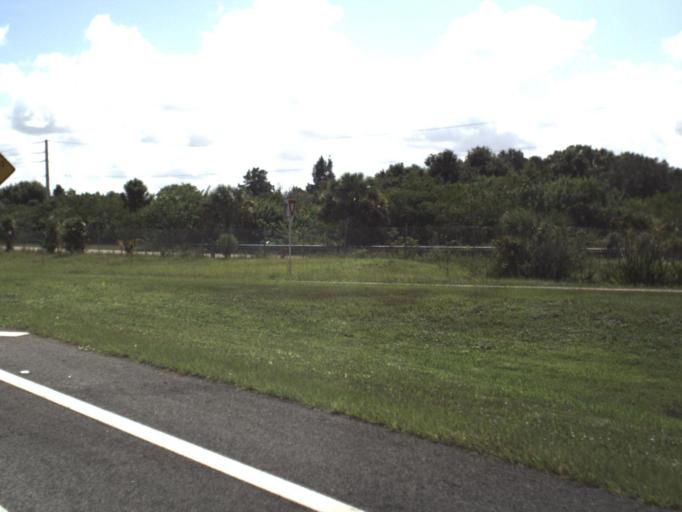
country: US
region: Florida
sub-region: Charlotte County
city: Punta Gorda
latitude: 26.9412
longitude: -82.0165
